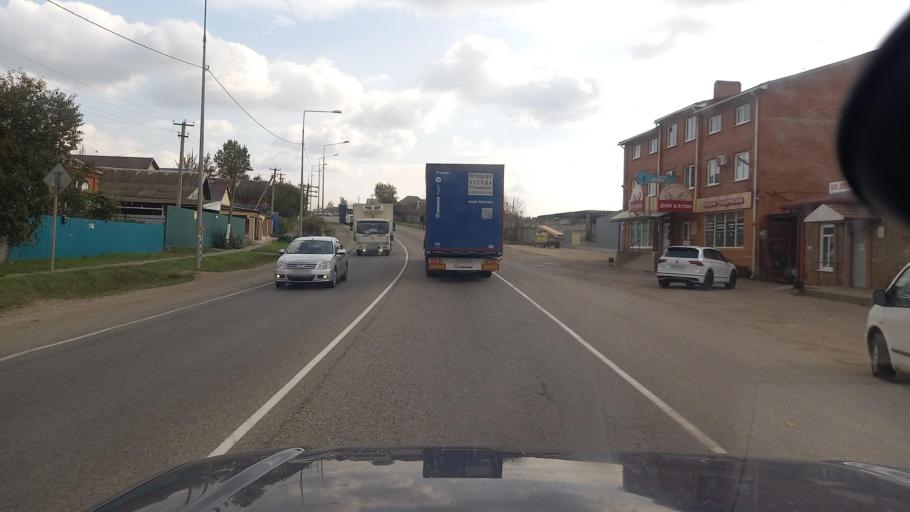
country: RU
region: Krasnodarskiy
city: Kholmskiy
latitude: 44.8489
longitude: 38.4045
